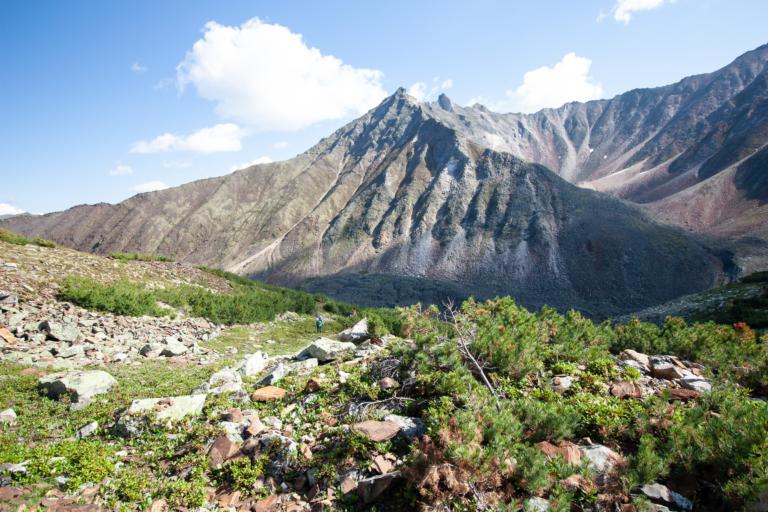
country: RU
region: Respublika Buryatiya
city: Novyy Uoyan
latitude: 56.2996
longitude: 111.2865
